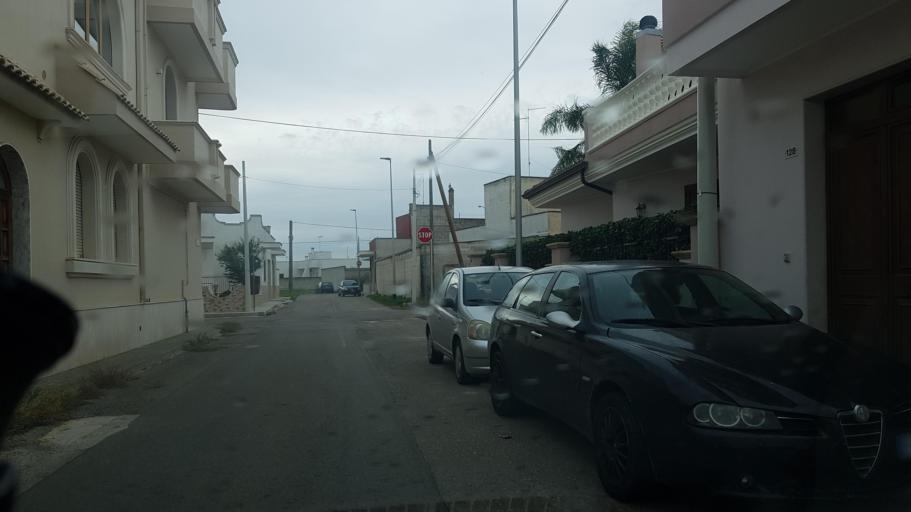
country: IT
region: Apulia
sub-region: Provincia di Lecce
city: Leverano
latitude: 40.2827
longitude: 17.9910
